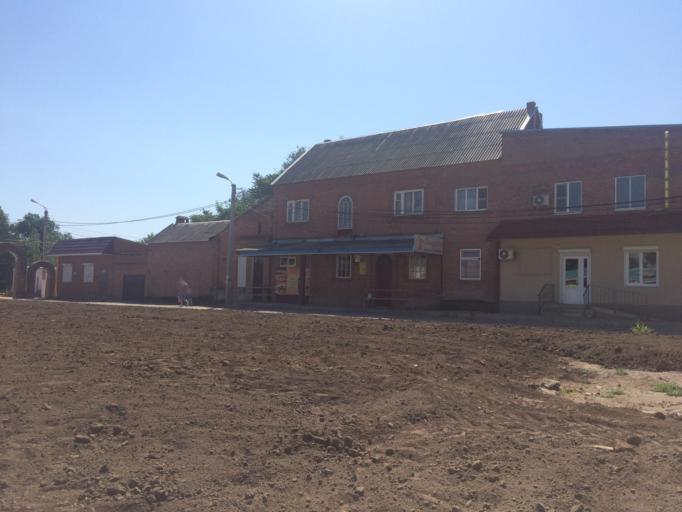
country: RU
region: Rostov
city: Sal'sk
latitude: 46.4744
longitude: 41.5440
